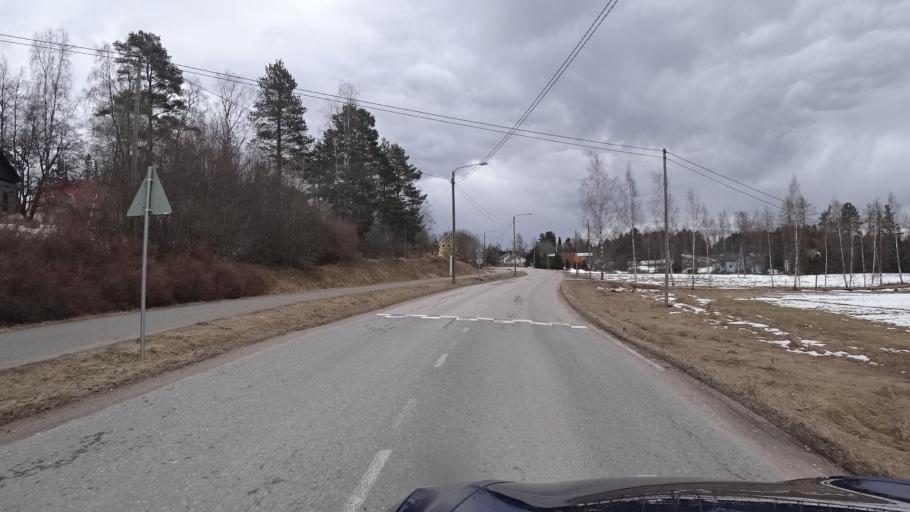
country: FI
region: Paijanne Tavastia
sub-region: Lahti
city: Nastola
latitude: 60.8739
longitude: 26.0054
